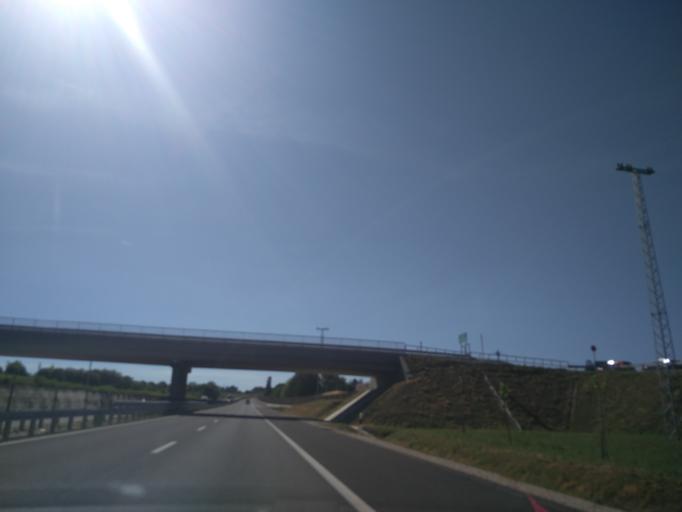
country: HU
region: Veszprem
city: Herend
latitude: 47.1303
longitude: 17.7497
